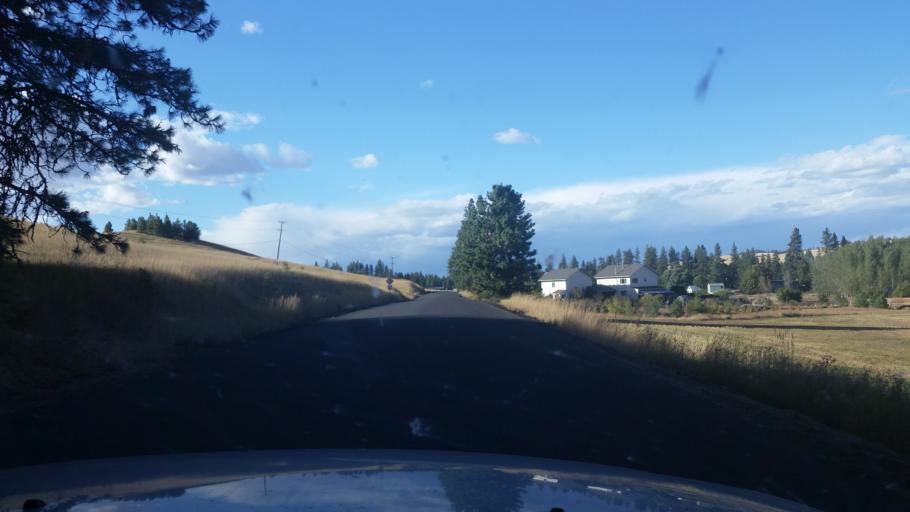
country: US
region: Washington
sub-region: Spokane County
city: Cheney
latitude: 47.5162
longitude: -117.5739
